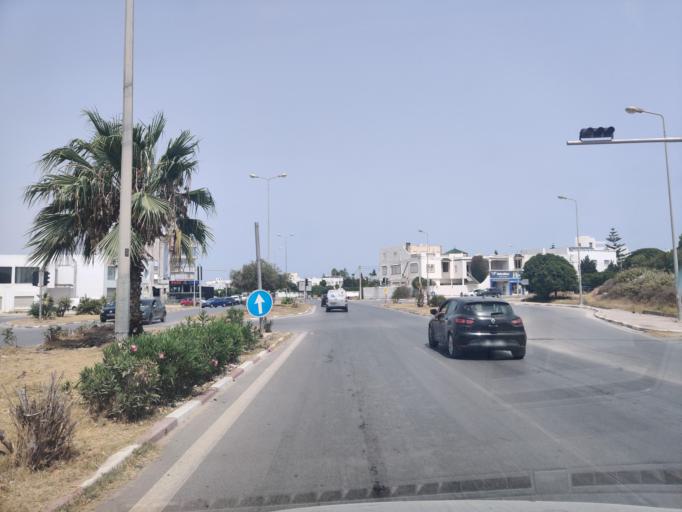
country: TN
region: Tunis
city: Carthage
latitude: 36.8639
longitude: 10.3160
